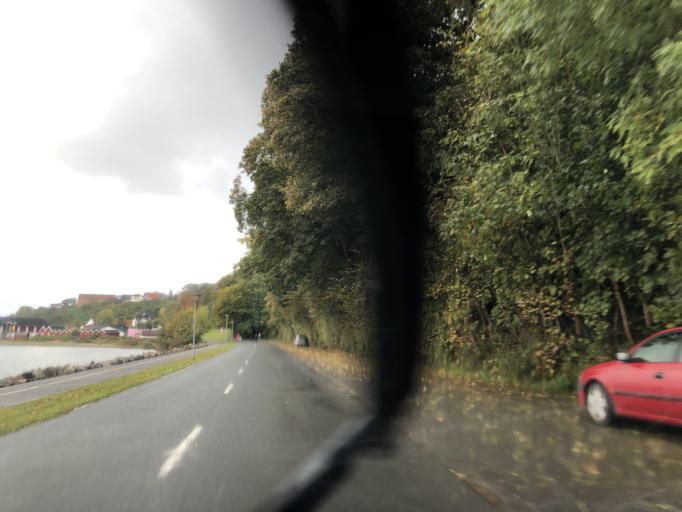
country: DK
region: Central Jutland
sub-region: Lemvig Kommune
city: Lemvig
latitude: 56.5522
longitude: 8.2970
